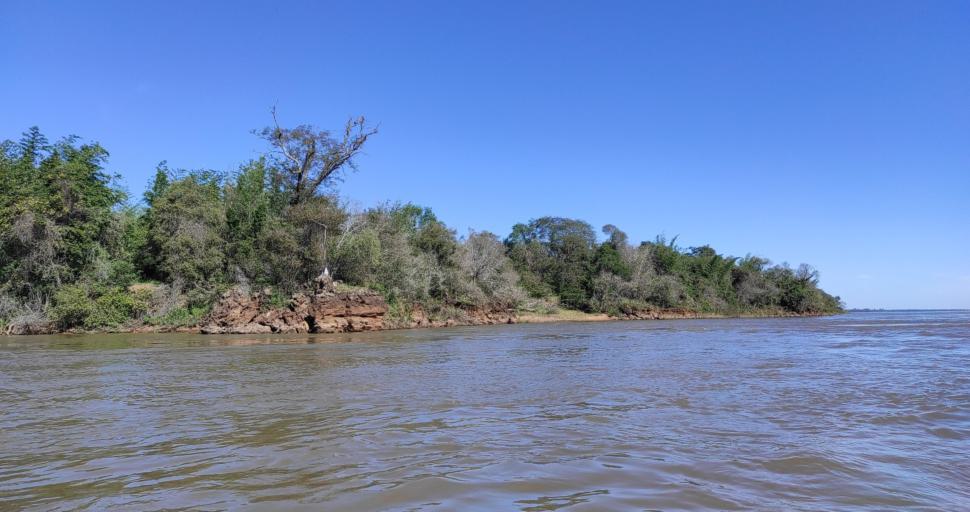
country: AR
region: Corrientes
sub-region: Departamento de Itati
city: Itati
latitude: -27.2795
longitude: -58.3253
